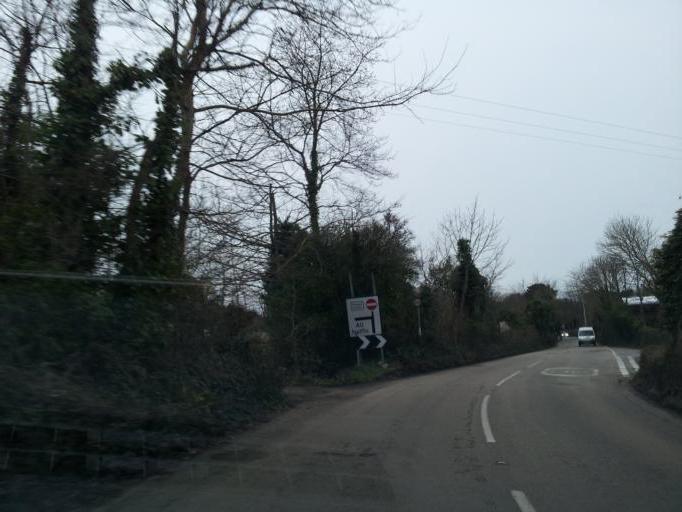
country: GB
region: England
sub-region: Cornwall
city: Redruth
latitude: 50.2398
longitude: -5.2385
